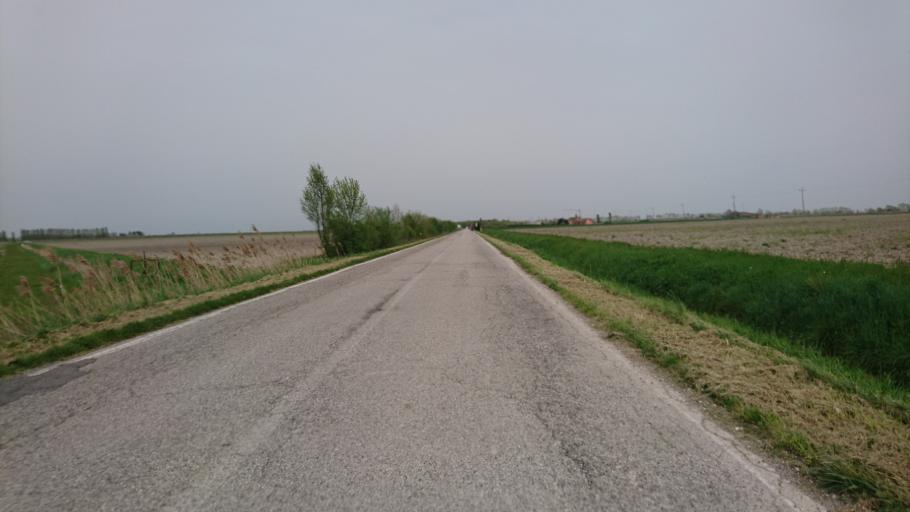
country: IT
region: Veneto
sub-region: Provincia di Venezia
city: La Salute di Livenza
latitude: 45.6785
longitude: 12.8499
